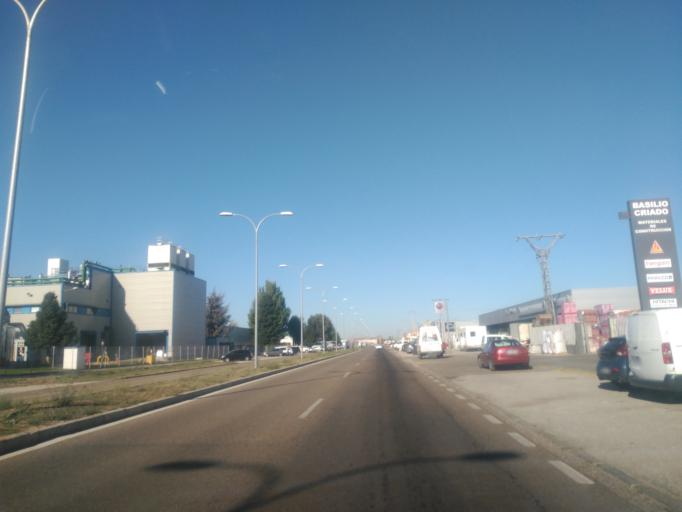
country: ES
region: Castille and Leon
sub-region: Provincia de Burgos
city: Aranda de Duero
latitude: 41.6652
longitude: -3.7091
